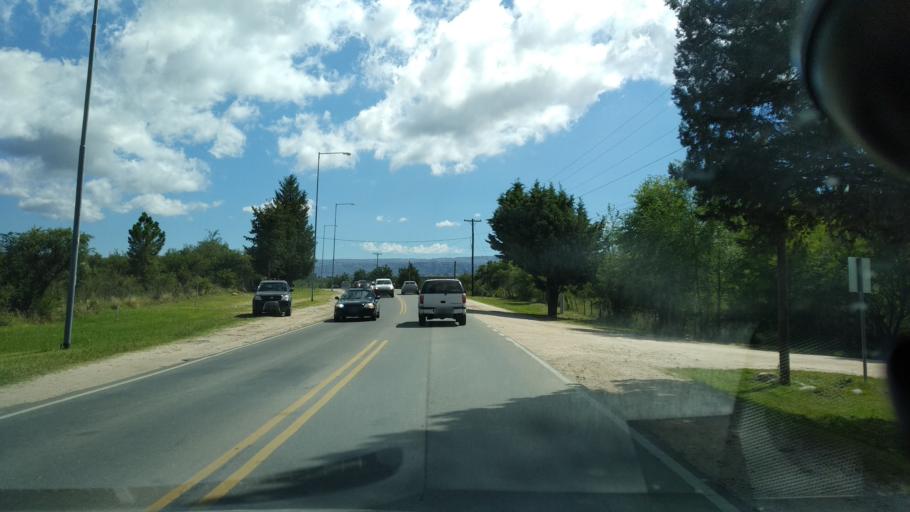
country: AR
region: Cordoba
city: Mina Clavero
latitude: -31.7906
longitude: -64.9990
